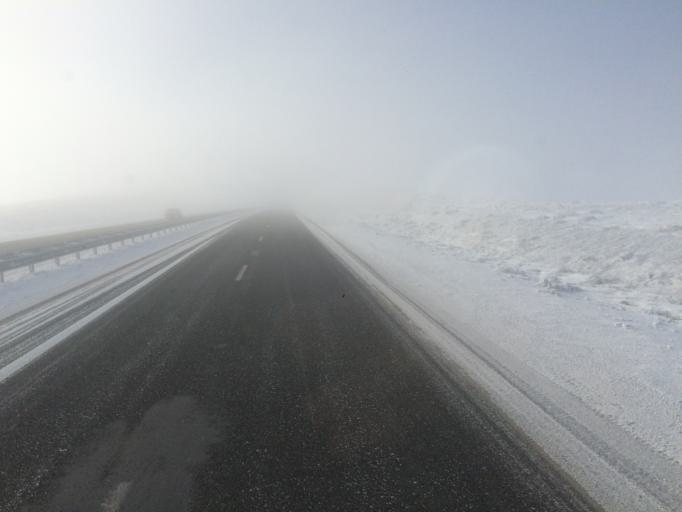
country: KZ
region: Zhambyl
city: Georgiyevka
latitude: 43.3963
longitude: 74.8261
